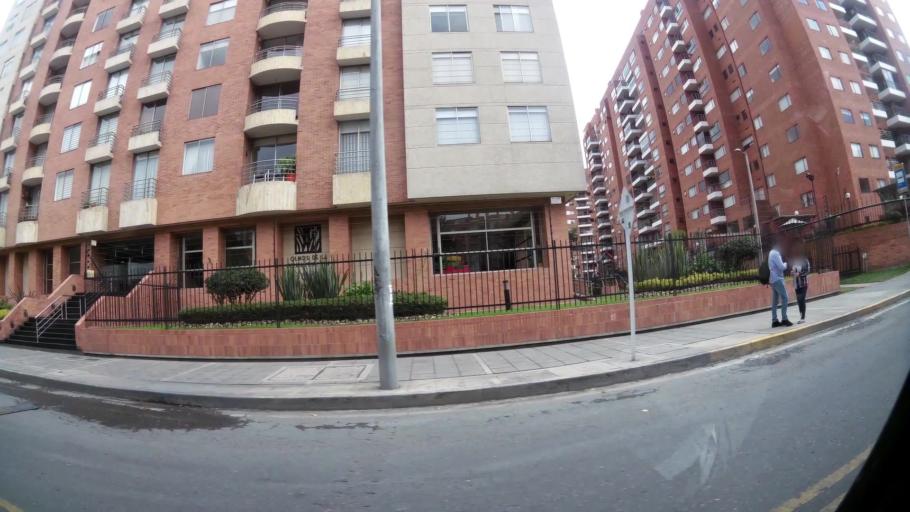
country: CO
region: Bogota D.C.
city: Barrio San Luis
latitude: 4.7342
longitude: -74.0574
